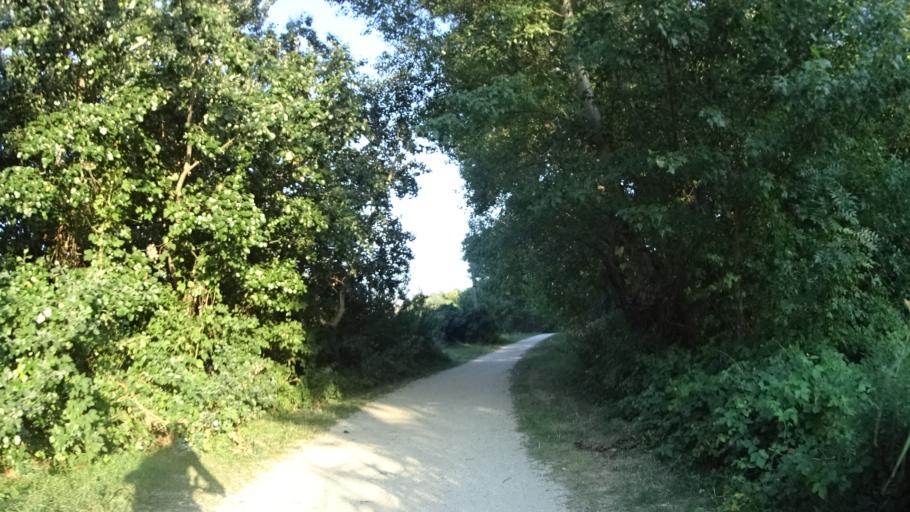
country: HU
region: Pest
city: Halasztelek
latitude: 47.3899
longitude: 18.9895
